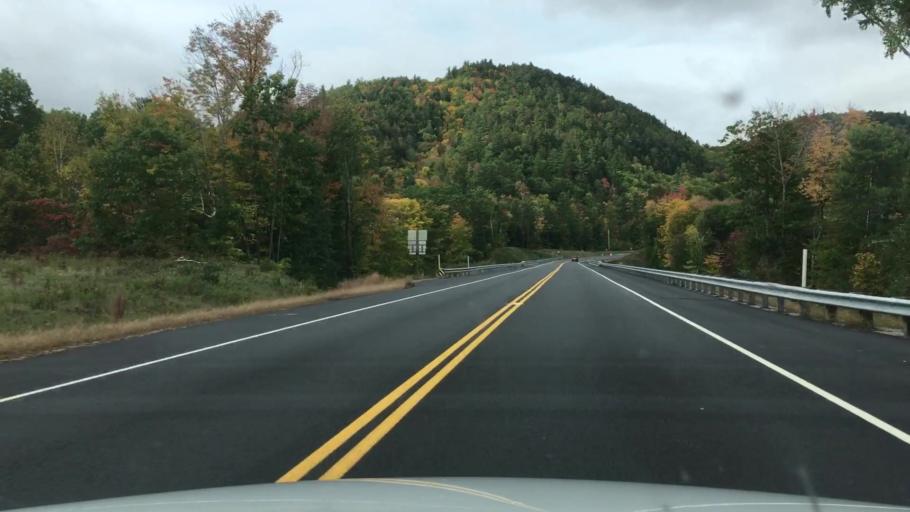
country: US
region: Maine
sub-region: Oxford County
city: Bethel
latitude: 44.3929
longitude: -70.9781
